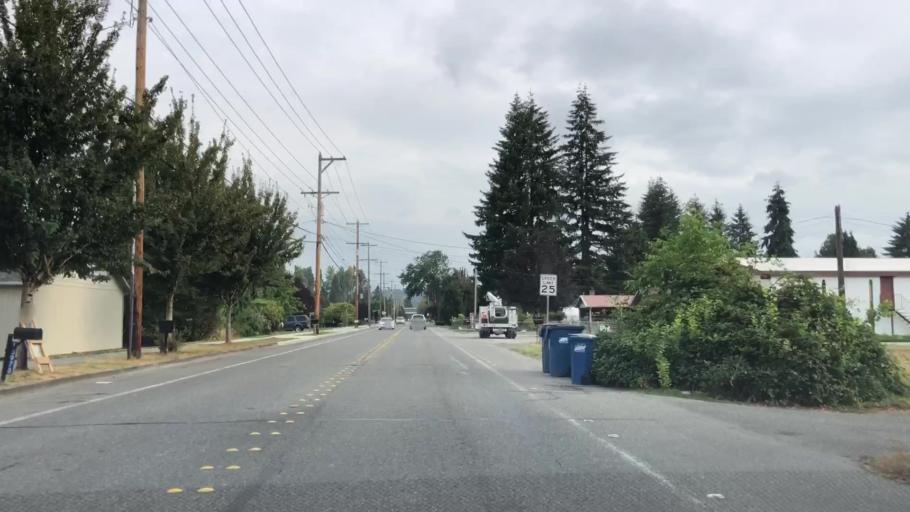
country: US
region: Washington
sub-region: Snohomish County
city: Monroe
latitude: 47.8524
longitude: -121.9905
